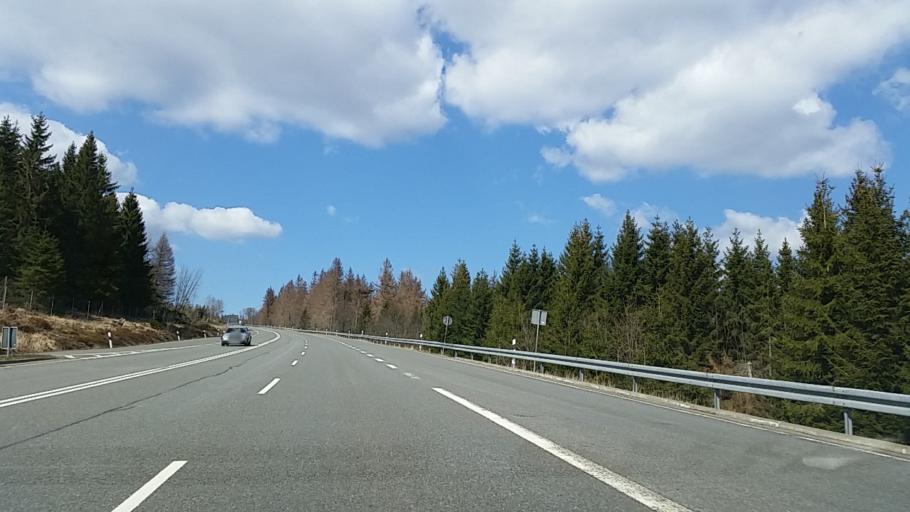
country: DE
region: Lower Saxony
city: Braunlage
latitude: 51.7412
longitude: 10.5873
